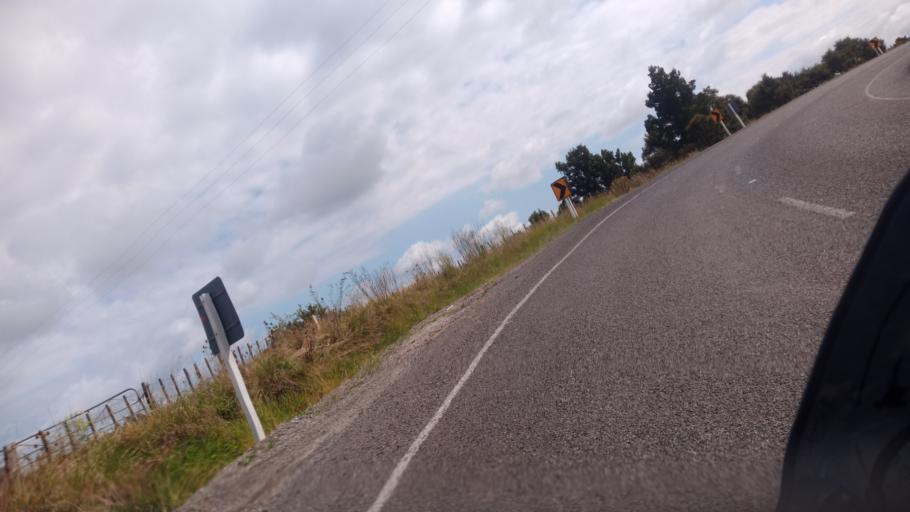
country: NZ
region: Gisborne
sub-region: Gisborne District
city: Gisborne
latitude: -38.1527
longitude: 178.2867
